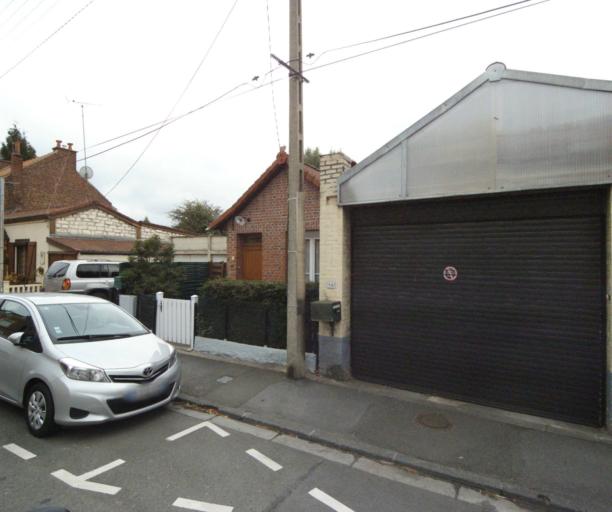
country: FR
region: Nord-Pas-de-Calais
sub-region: Departement du Nord
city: Lezennes
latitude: 50.6138
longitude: 3.1205
